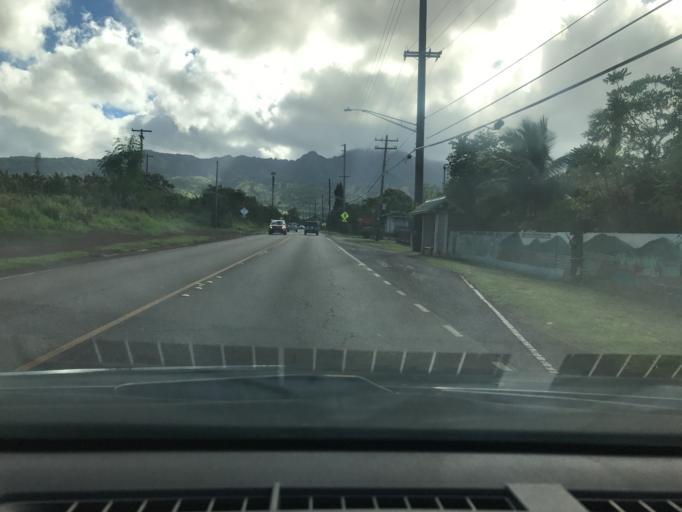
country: US
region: Hawaii
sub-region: Honolulu County
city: Hale'iwa
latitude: 21.5730
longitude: -158.1076
